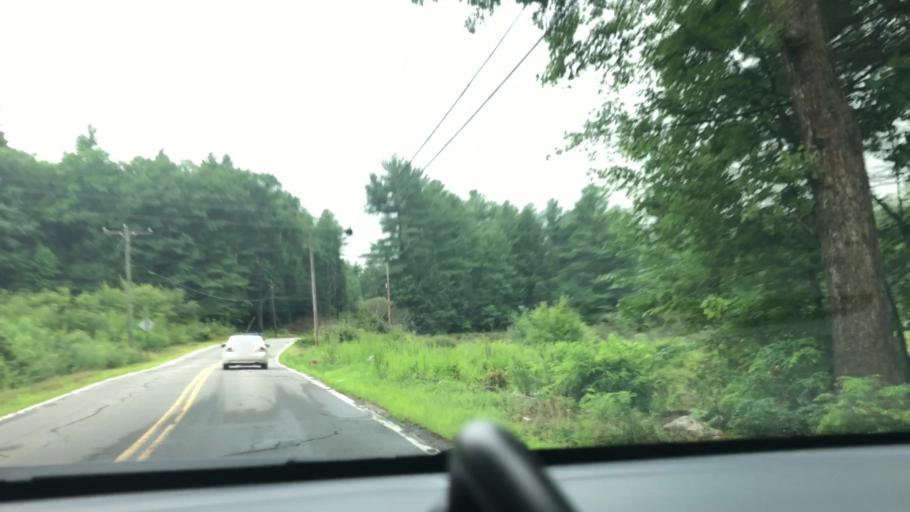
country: US
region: New Hampshire
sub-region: Hillsborough County
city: Pinardville
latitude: 42.9901
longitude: -71.5280
